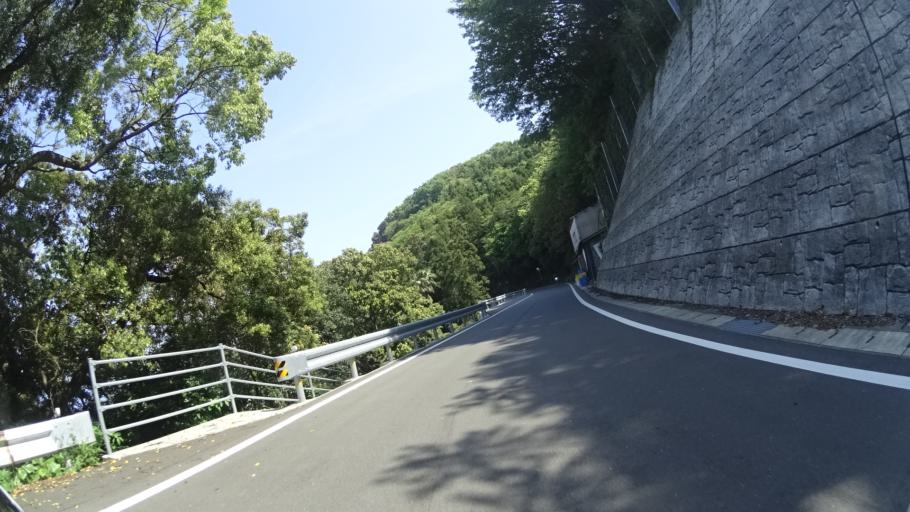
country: JP
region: Oita
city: Tsukumiura
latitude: 33.3543
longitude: 132.0319
